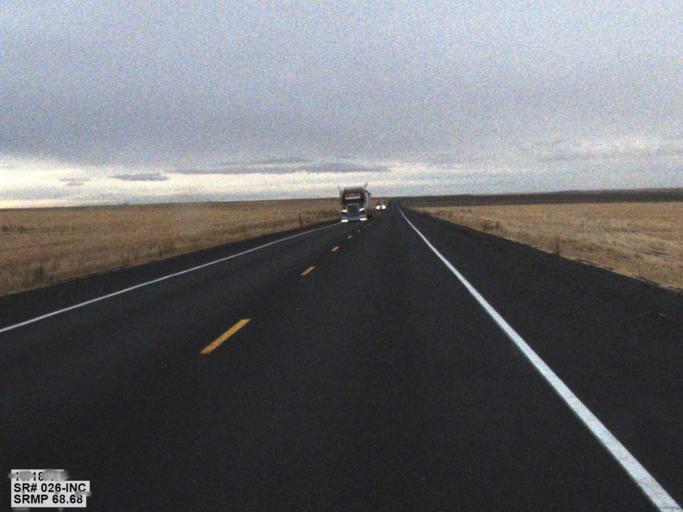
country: US
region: Washington
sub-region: Franklin County
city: Connell
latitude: 46.7946
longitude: -118.5876
